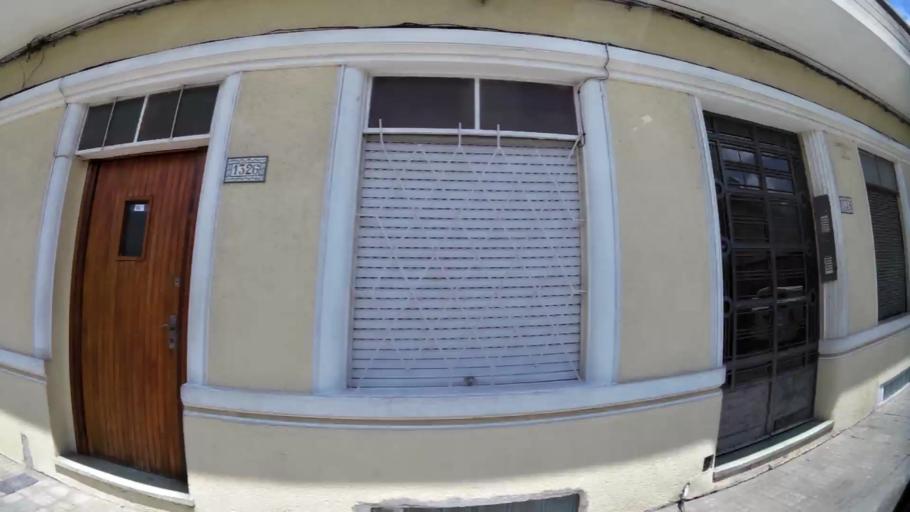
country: UY
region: Montevideo
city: Montevideo
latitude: -34.8693
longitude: -56.1942
